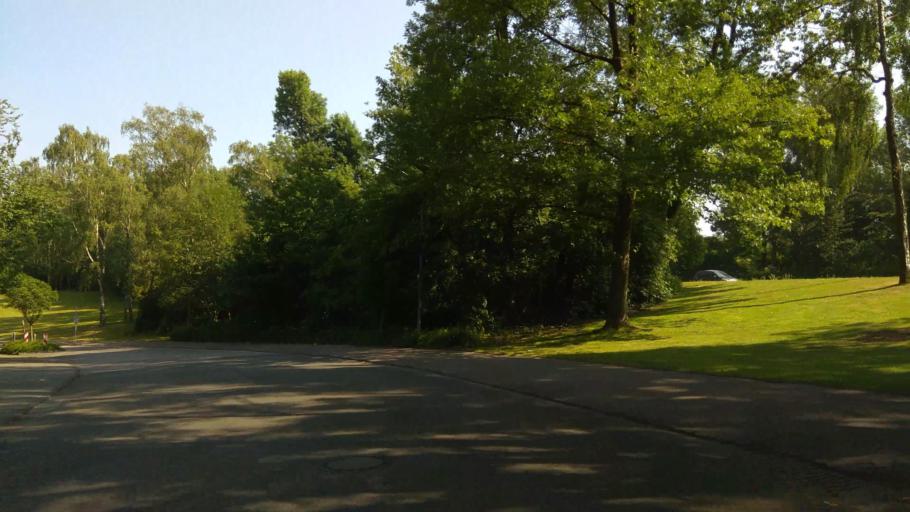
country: DE
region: North Rhine-Westphalia
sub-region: Regierungsbezirk Munster
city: Gladbeck
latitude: 51.5654
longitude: 7.0579
